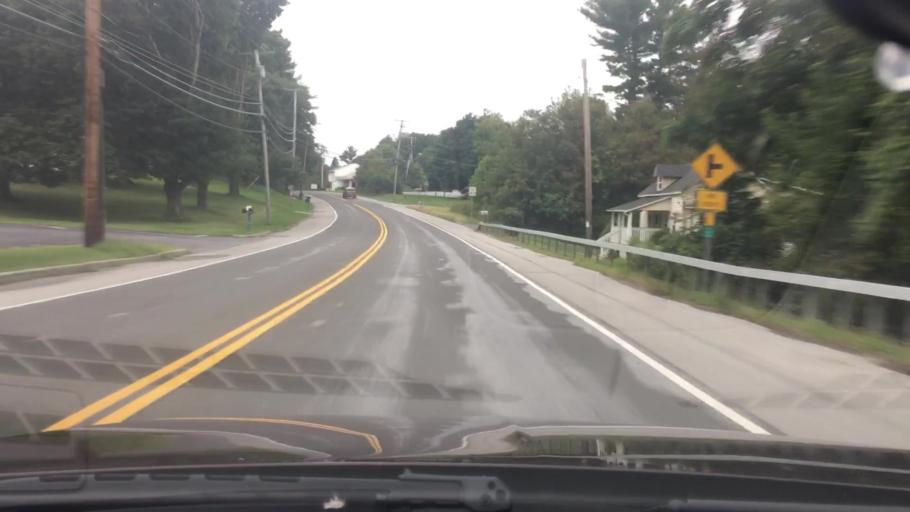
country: US
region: New York
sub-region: Dutchess County
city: Pleasant Valley
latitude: 41.7178
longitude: -73.8551
